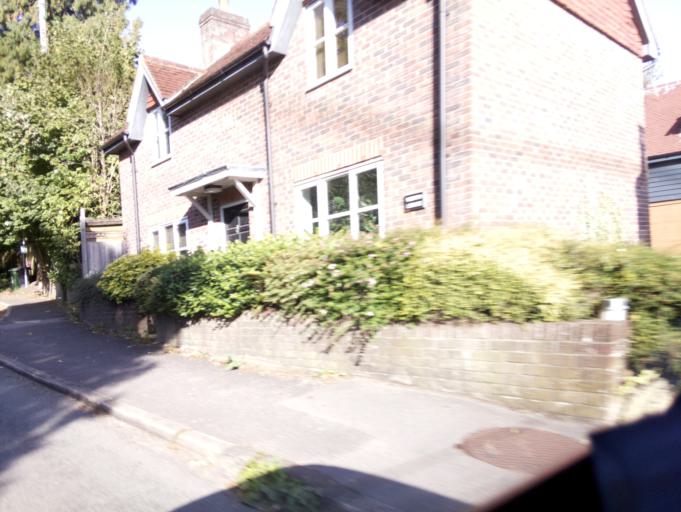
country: GB
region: England
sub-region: Hampshire
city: Four Marks
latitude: 51.0127
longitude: -1.0867
